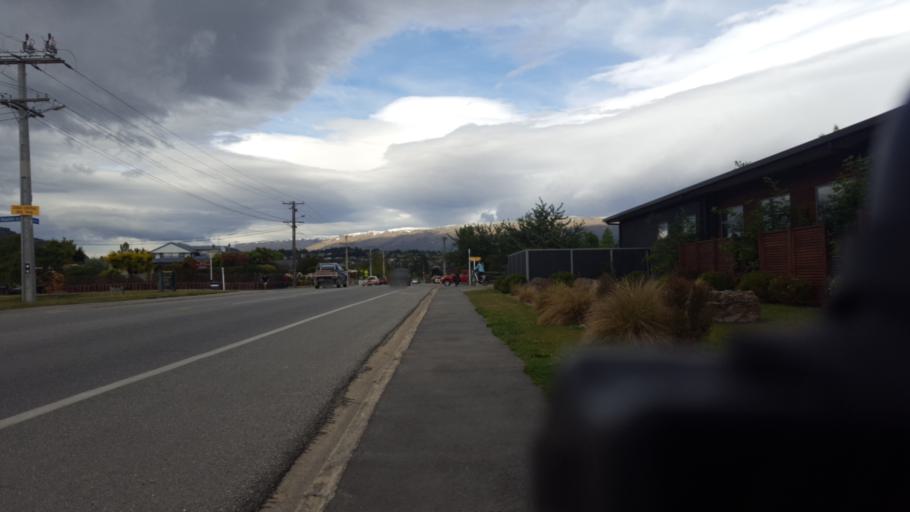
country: NZ
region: Otago
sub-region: Queenstown-Lakes District
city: Wanaka
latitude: -45.2487
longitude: 169.3991
